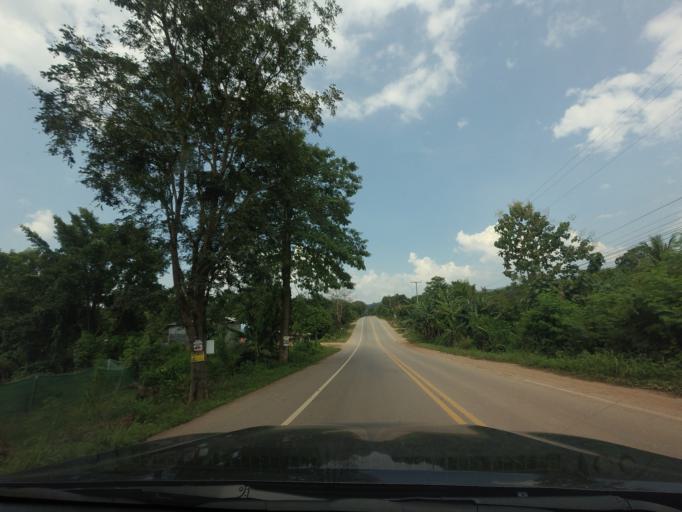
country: TH
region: Phitsanulok
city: Nakhon Thai
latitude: 17.0217
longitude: 100.9310
